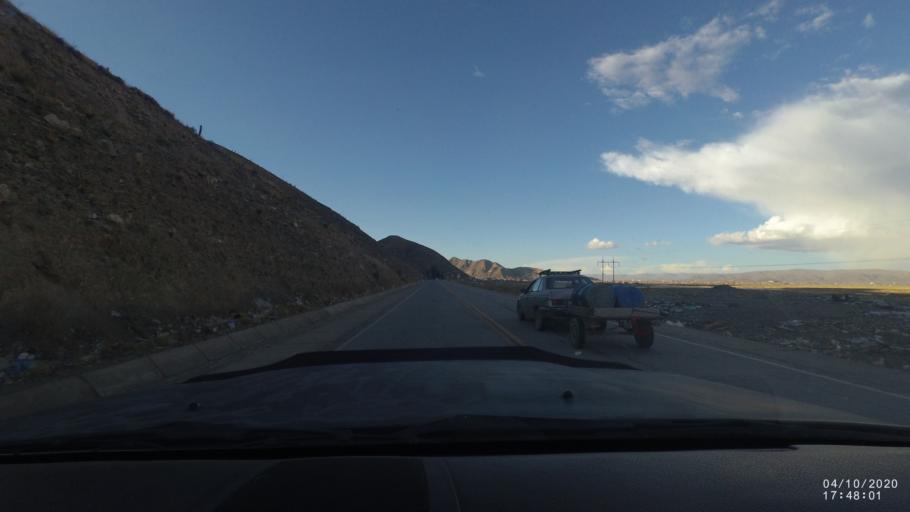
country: BO
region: Oruro
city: Oruro
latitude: -18.0213
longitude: -67.1397
